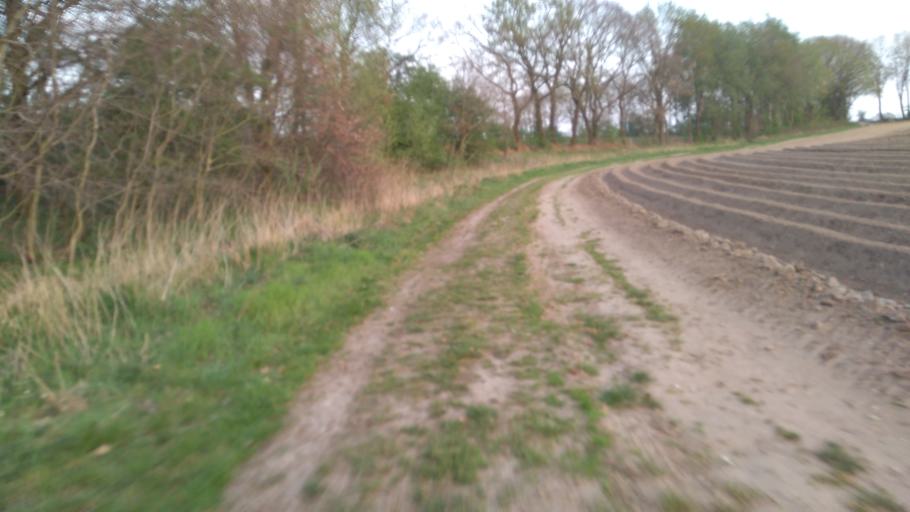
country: DE
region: Lower Saxony
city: Bliedersdorf
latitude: 53.4780
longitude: 9.5471
